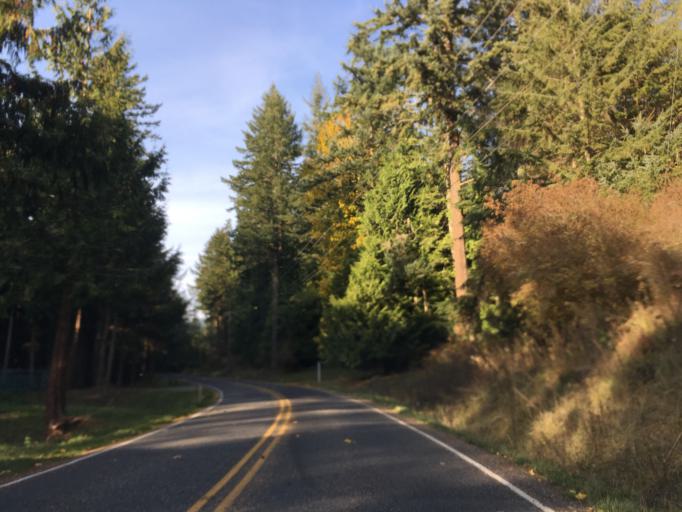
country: US
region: Washington
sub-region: San Juan County
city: Friday Harbor
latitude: 48.6310
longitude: -122.8337
